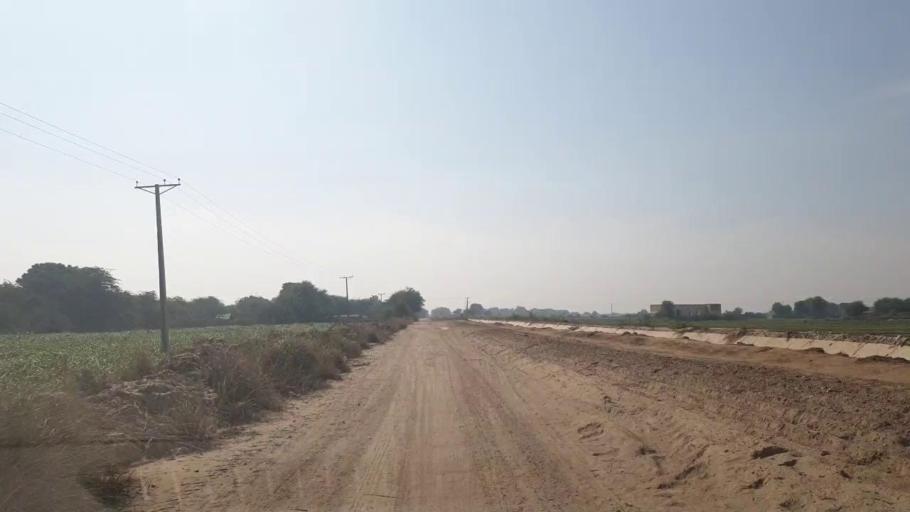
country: PK
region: Sindh
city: Matiari
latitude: 25.6661
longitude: 68.3459
